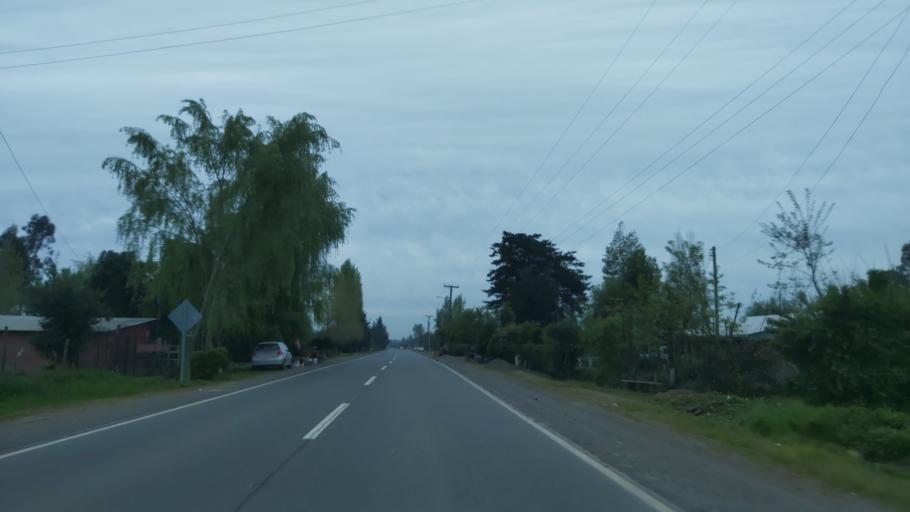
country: CL
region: Maule
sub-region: Provincia de Linares
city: Linares
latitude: -35.7693
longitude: -71.5142
